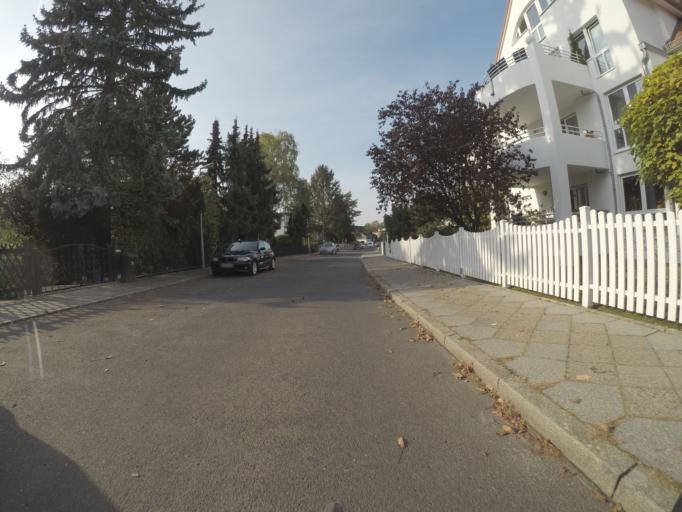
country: DE
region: Berlin
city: Britz
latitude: 52.4186
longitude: 13.4307
